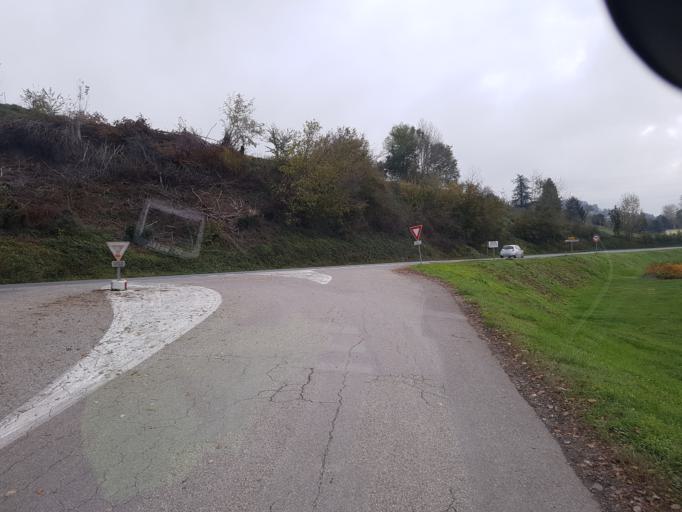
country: FR
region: Rhone-Alpes
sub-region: Departement de la Savoie
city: Saint-Genix-sur-Guiers
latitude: 45.5955
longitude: 5.6366
